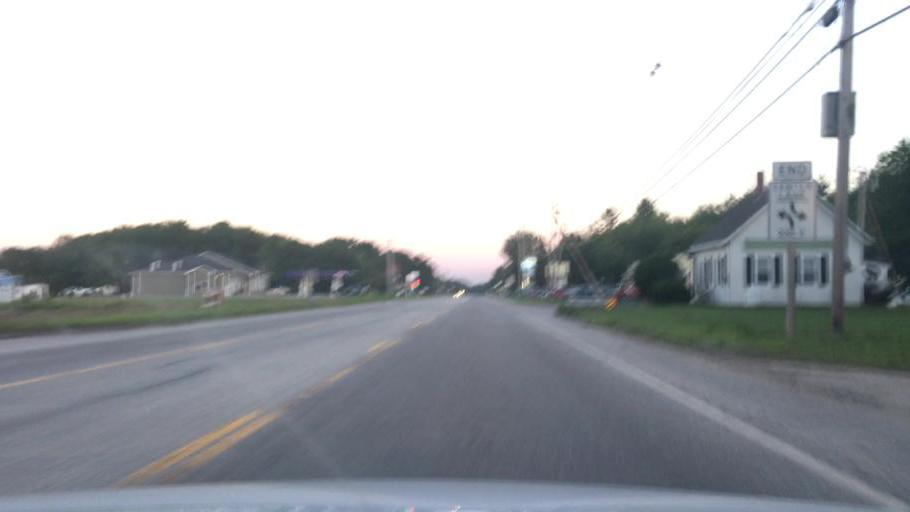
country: US
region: Maine
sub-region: Androscoggin County
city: Turner
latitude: 44.1900
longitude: -70.2385
